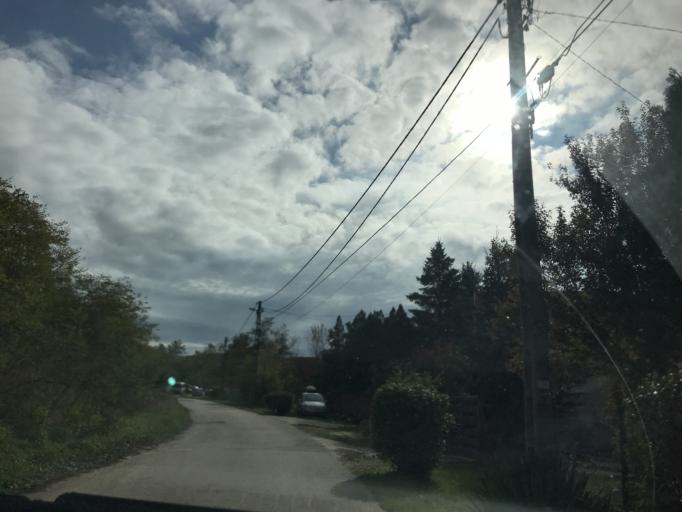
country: HU
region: Komarom-Esztergom
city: Piliscsev
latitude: 47.6726
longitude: 18.7939
